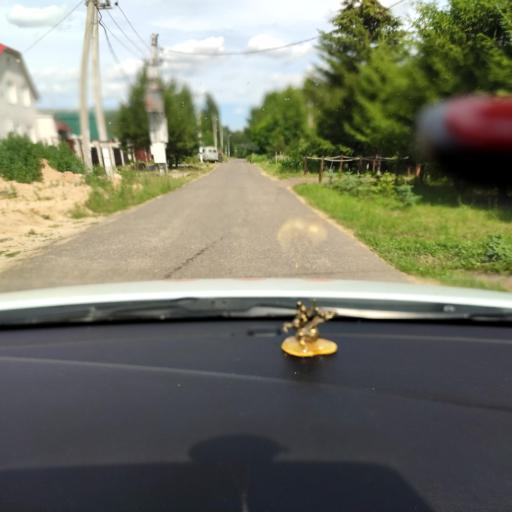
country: RU
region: Tatarstan
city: Stolbishchi
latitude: 55.6335
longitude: 49.1377
